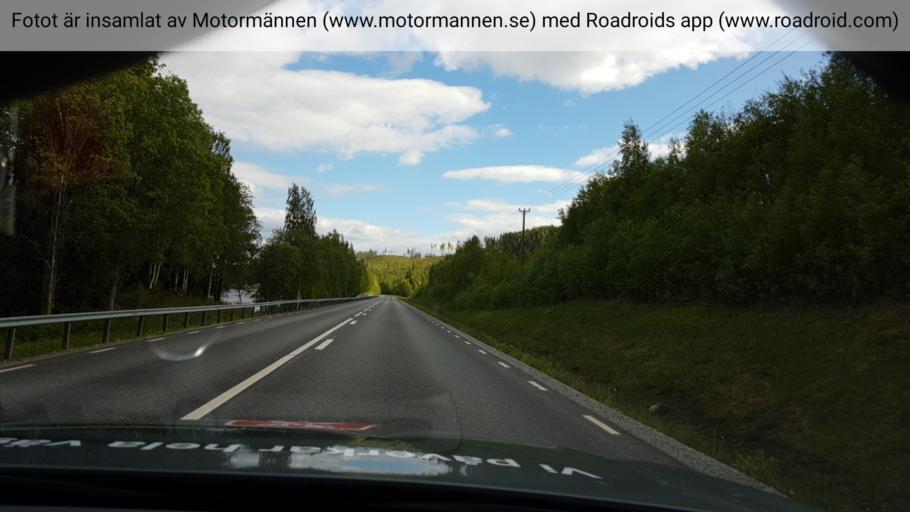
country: SE
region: Jaemtland
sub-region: Stroemsunds Kommun
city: Stroemsund
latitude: 64.1799
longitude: 15.6568
